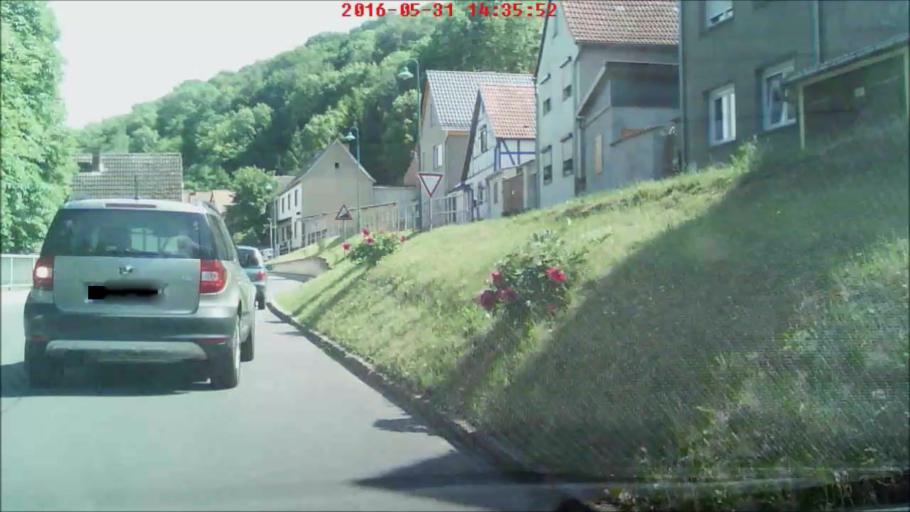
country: DE
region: Thuringia
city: Oberbosa
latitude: 51.3065
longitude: 11.0492
